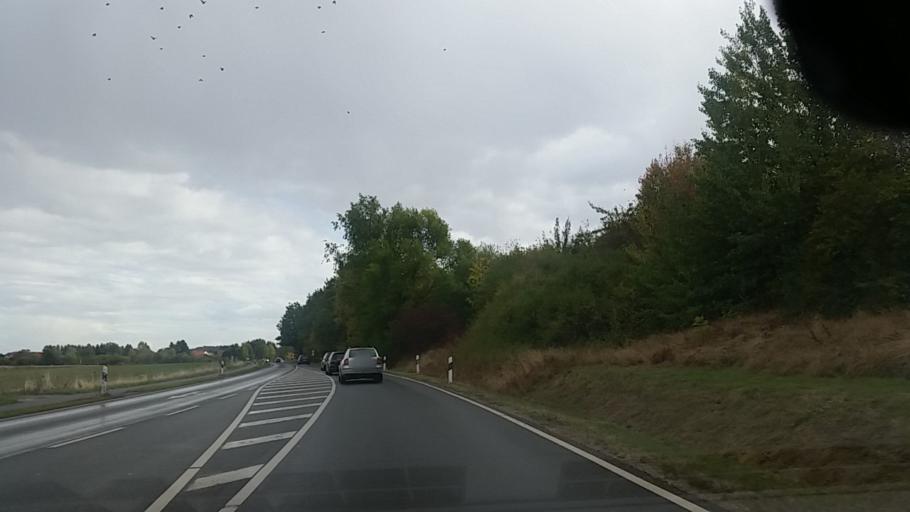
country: DE
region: Lower Saxony
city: Wolfsburg
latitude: 52.3962
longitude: 10.8398
